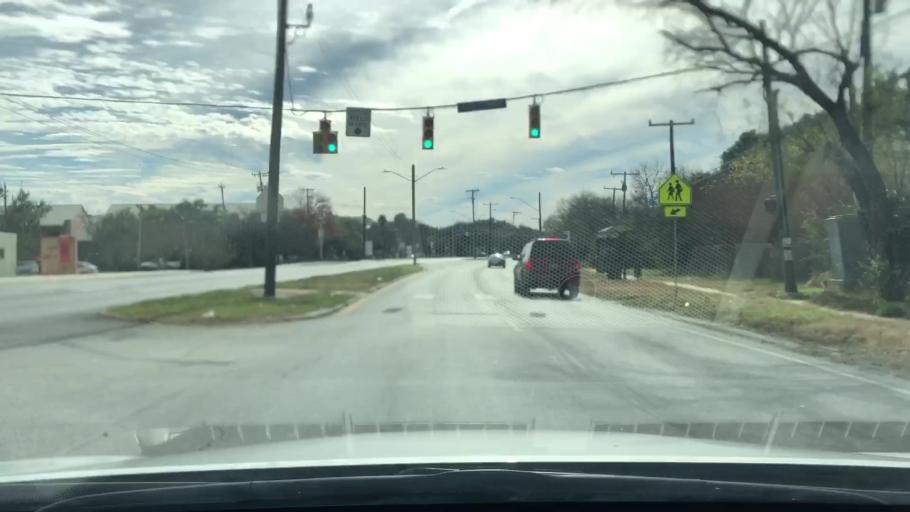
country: US
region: Texas
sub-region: Bexar County
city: Terrell Hills
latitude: 29.5112
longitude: -98.4349
